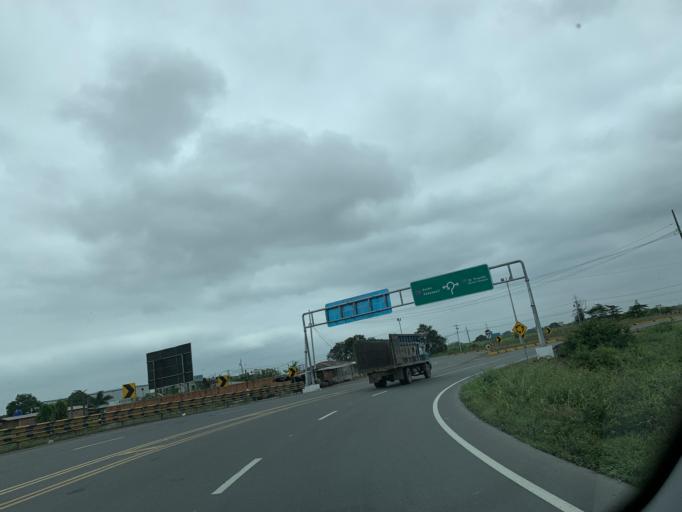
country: EC
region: Guayas
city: Coronel Marcelino Mariduena
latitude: -2.3302
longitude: -79.4180
